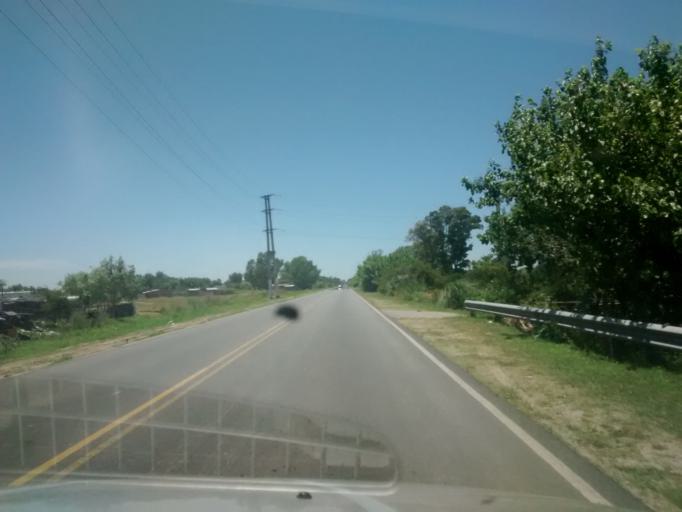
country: AR
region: Buenos Aires
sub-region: Partido de Berisso
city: Berisso
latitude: -34.8855
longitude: -57.8585
